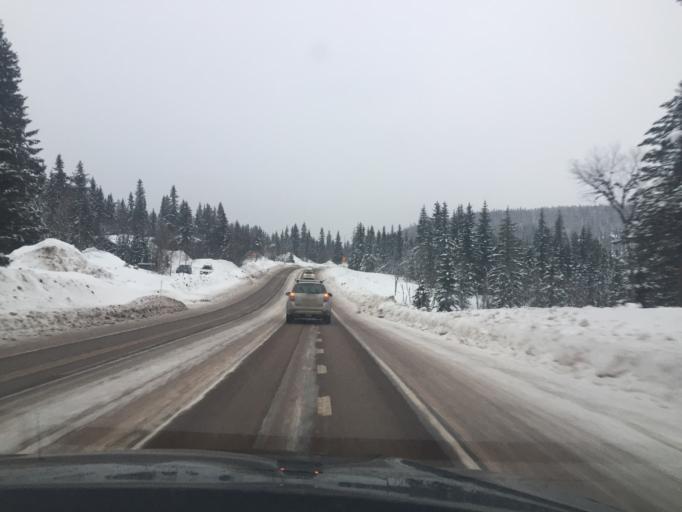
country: SE
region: Dalarna
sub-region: Malung-Saelens kommun
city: Malung
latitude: 61.1593
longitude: 13.1372
